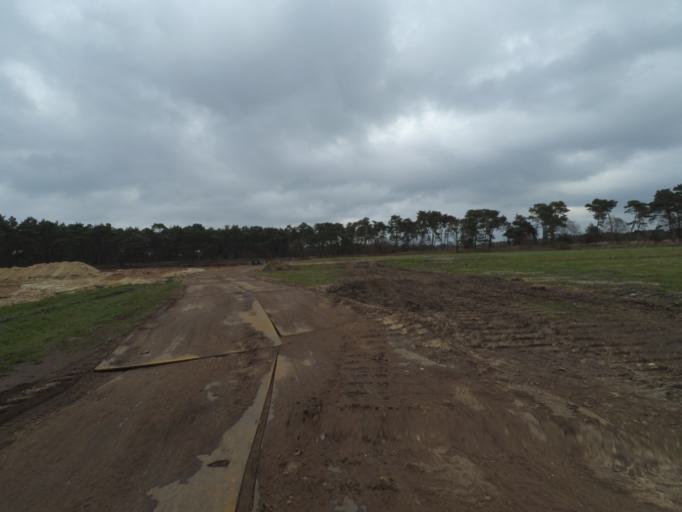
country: NL
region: Utrecht
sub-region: Gemeente Amersfoort
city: Amersfoort
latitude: 52.1203
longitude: 5.3790
